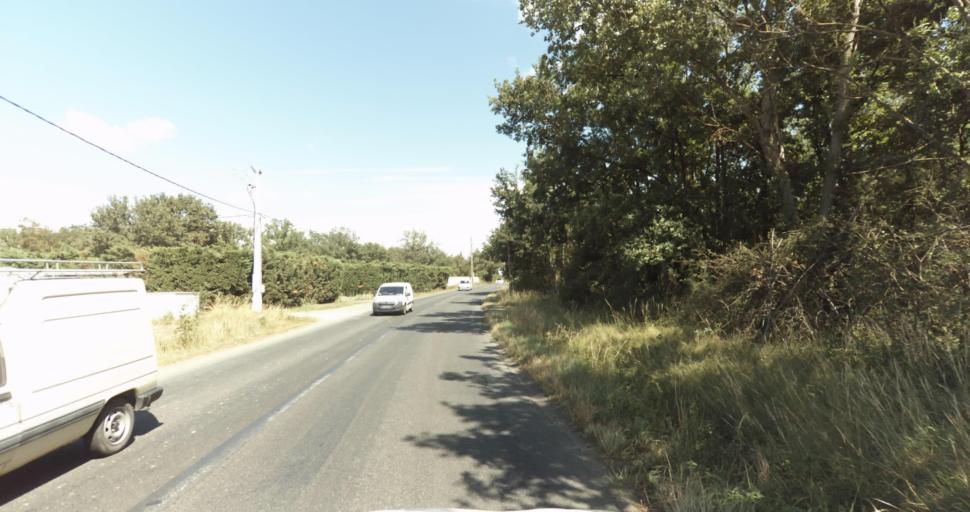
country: FR
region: Rhone-Alpes
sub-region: Departement du Rhone
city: Chaponost
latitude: 45.7123
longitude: 4.7205
